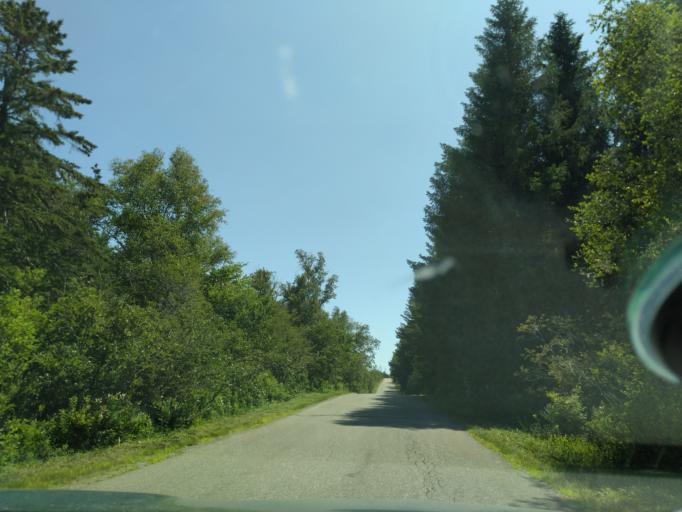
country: US
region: Maine
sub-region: Washington County
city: Eastport
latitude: 44.8333
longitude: -67.0082
